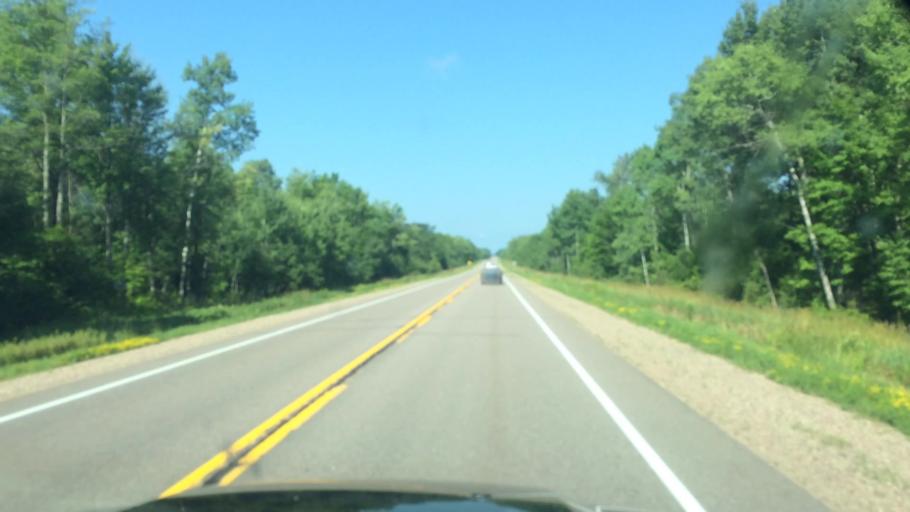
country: US
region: Wisconsin
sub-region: Langlade County
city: Antigo
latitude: 45.1468
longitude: -89.3556
